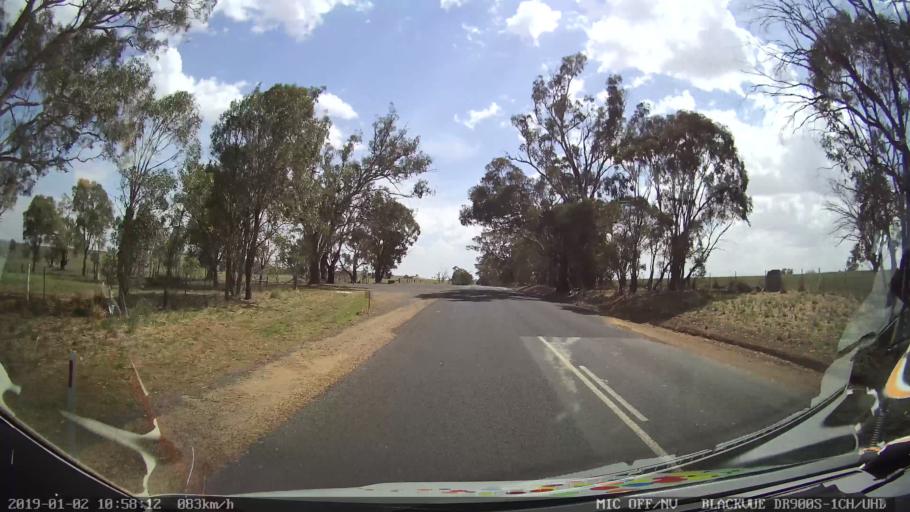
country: AU
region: New South Wales
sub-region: Cootamundra
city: Cootamundra
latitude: -34.6270
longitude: 148.2891
